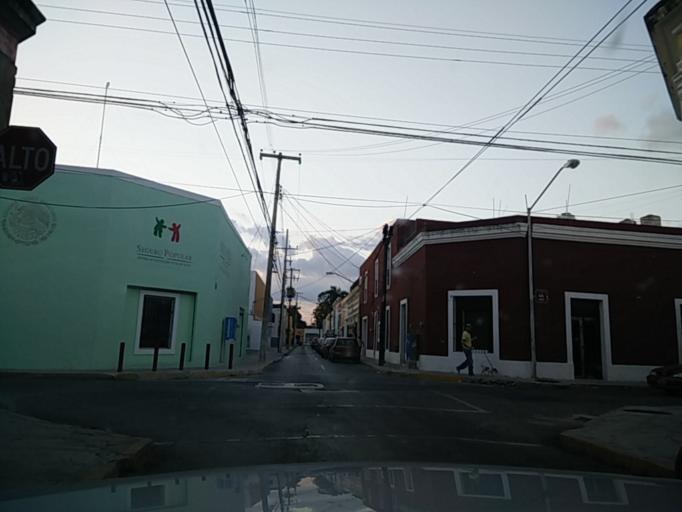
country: MX
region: Yucatan
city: Merida
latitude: 20.9729
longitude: -89.6259
